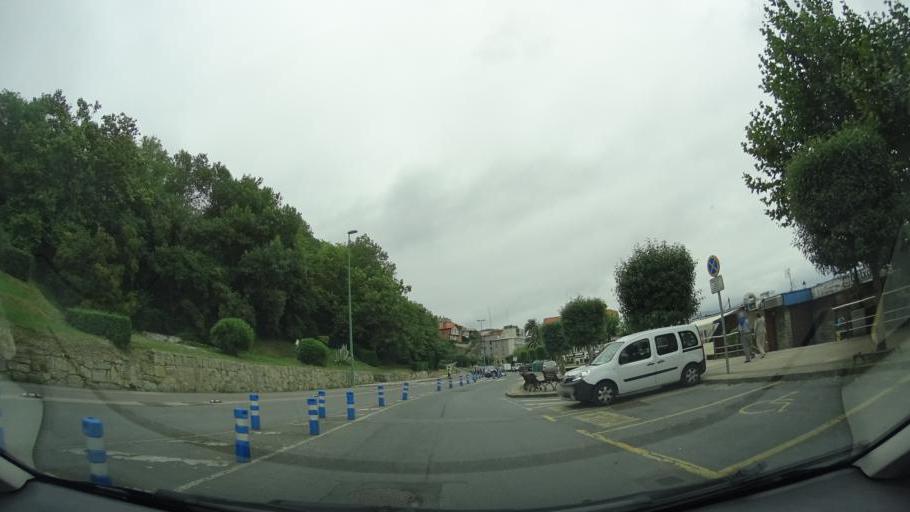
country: ES
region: Basque Country
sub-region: Bizkaia
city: Algorta
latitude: 43.3454
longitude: -3.0114
